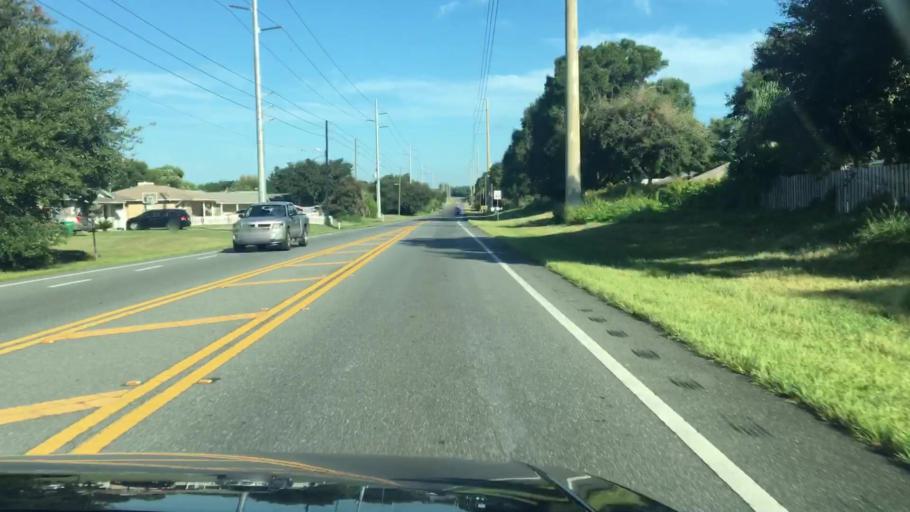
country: US
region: Florida
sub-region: Lake County
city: Eustis
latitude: 28.8776
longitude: -81.7116
